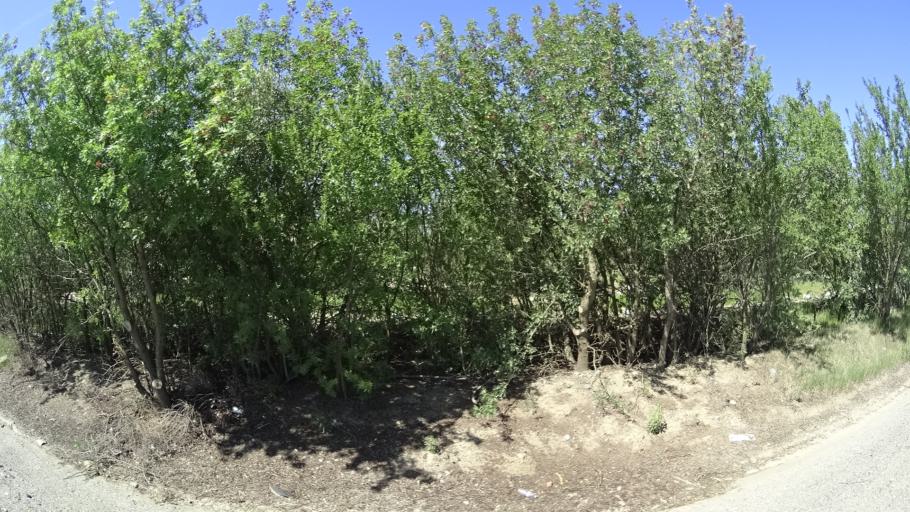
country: US
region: California
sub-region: Glenn County
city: Orland
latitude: 39.7066
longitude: -122.1408
